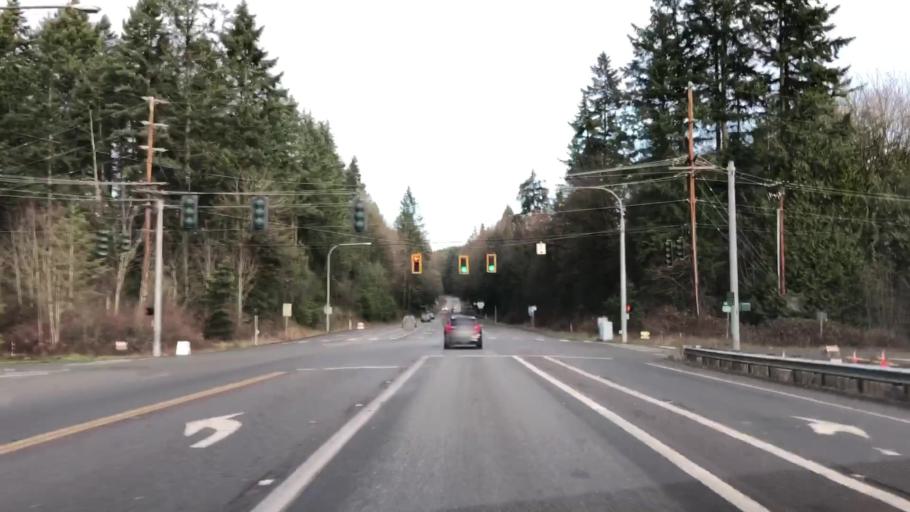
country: US
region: Washington
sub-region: Kitsap County
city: Bainbridge Island
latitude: 47.6534
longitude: -122.5233
